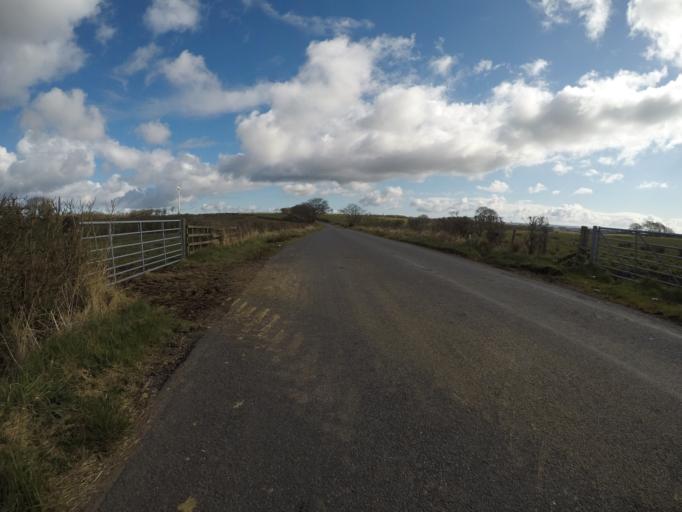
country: GB
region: Scotland
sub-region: North Ayrshire
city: Kilwinning
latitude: 55.6759
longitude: -4.6576
